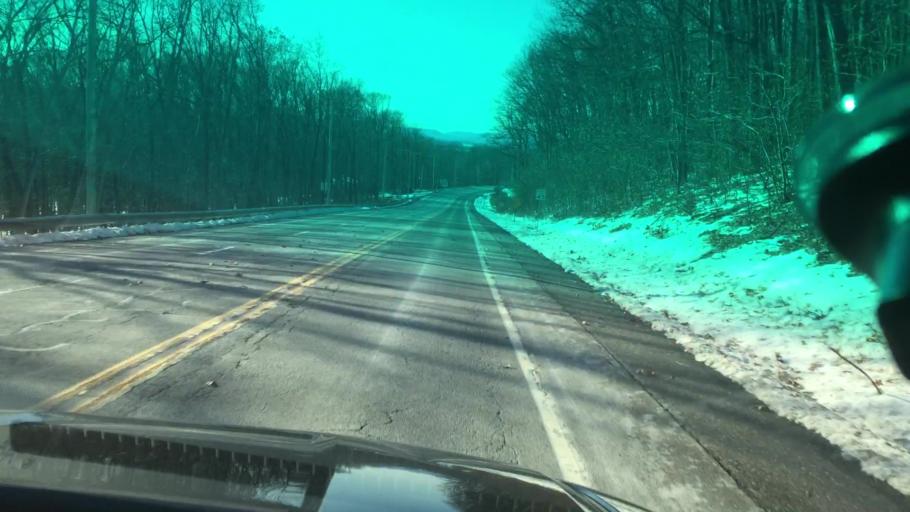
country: US
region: Pennsylvania
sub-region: Luzerne County
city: Oakdale
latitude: 41.0182
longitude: -75.9449
